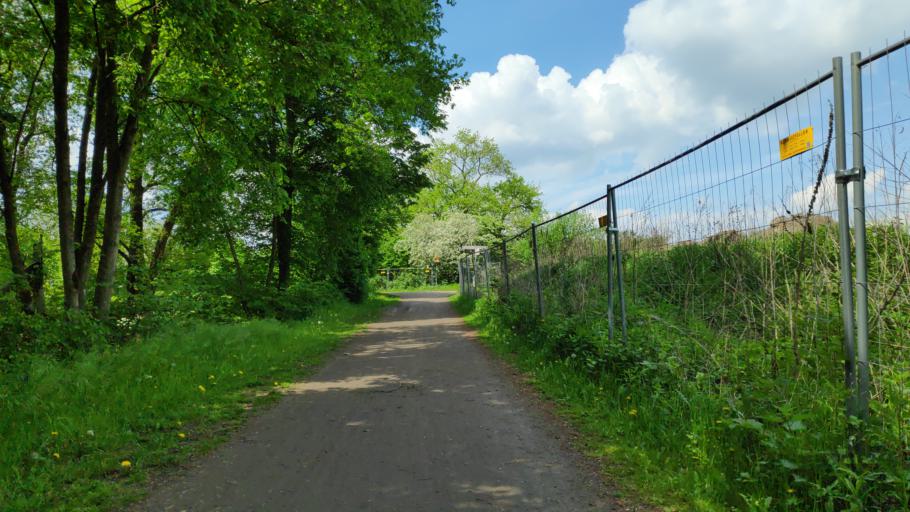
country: DE
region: North Rhine-Westphalia
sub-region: Regierungsbezirk Munster
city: Gelsenkirchen
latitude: 51.5519
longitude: 7.1233
